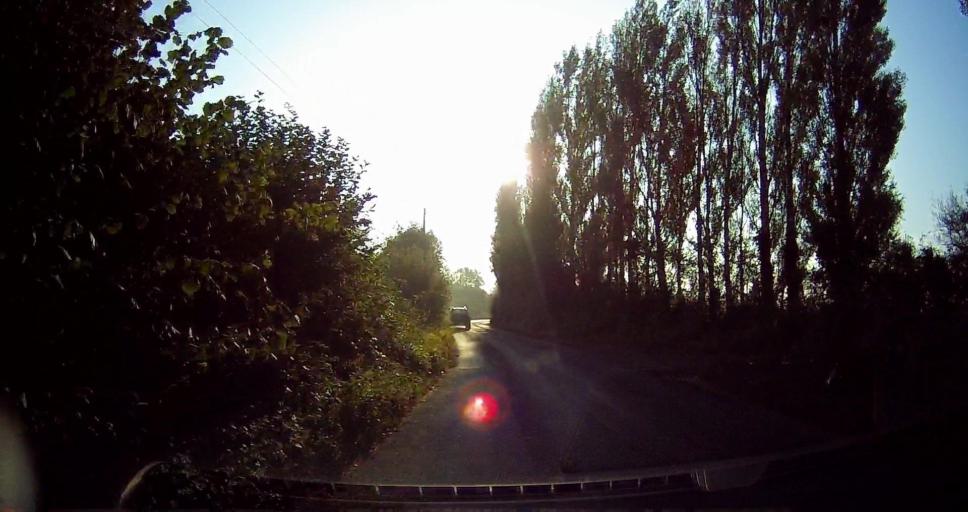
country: GB
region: England
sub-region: Kent
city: Kennington
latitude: 51.1869
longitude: 0.8998
